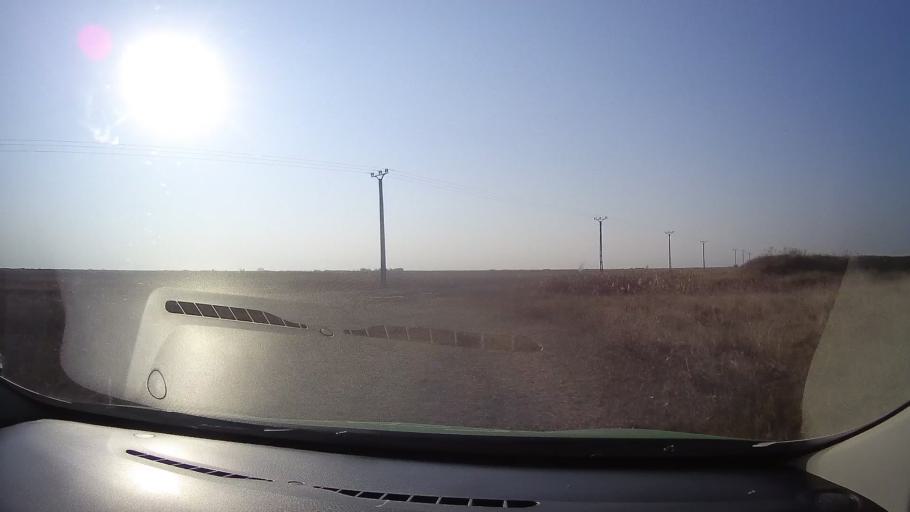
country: RO
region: Arad
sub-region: Comuna Pilu
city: Pilu
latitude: 46.5525
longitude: 21.3342
